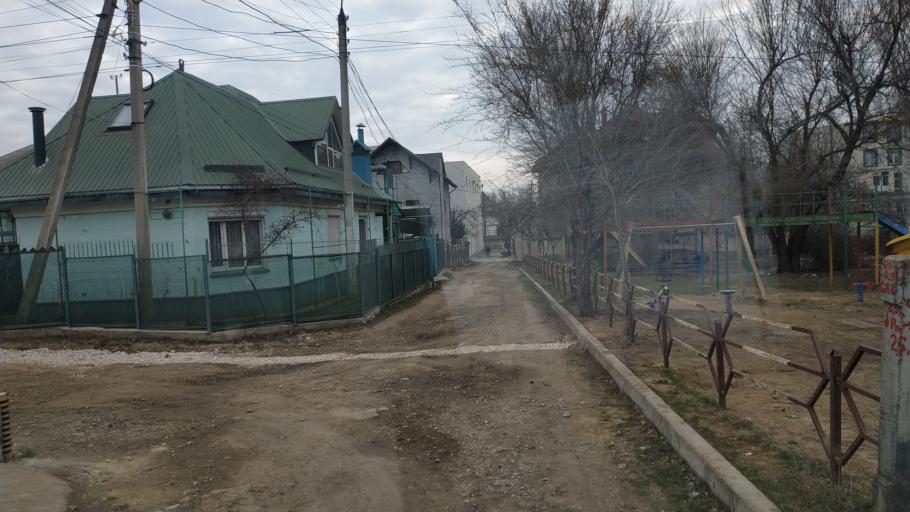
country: MD
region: Chisinau
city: Vatra
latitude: 47.0286
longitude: 28.7865
